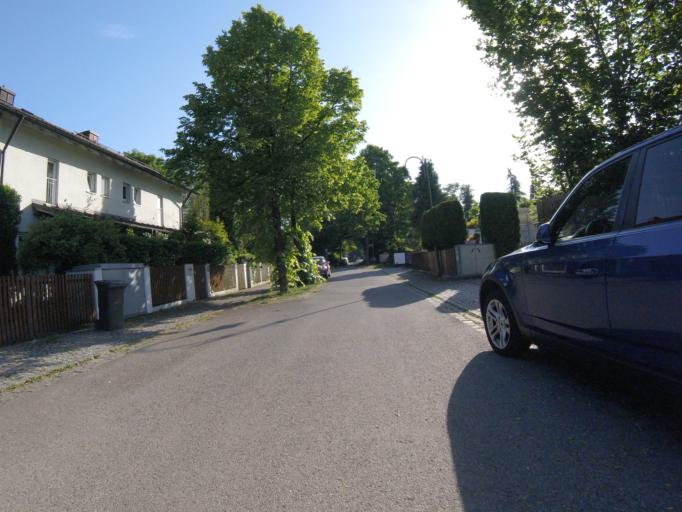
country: DE
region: Bavaria
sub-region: Upper Bavaria
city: Ottobrunn
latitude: 48.0619
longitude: 11.6659
